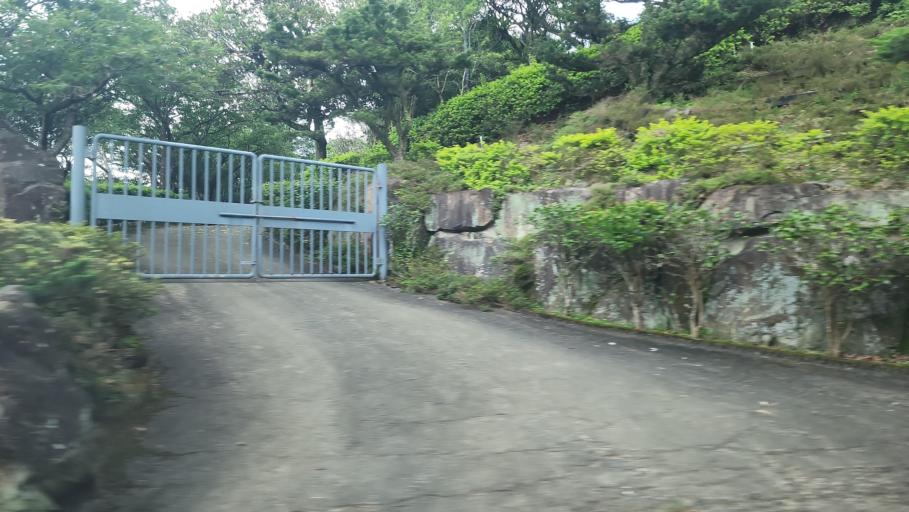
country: TW
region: Taiwan
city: Daxi
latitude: 24.8858
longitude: 121.4189
